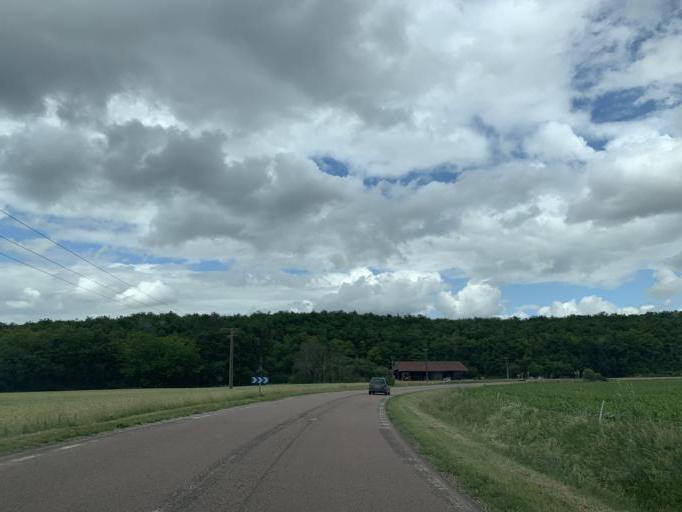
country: FR
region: Bourgogne
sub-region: Departement de l'Yonne
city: Chablis
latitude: 47.7446
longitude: 3.8263
